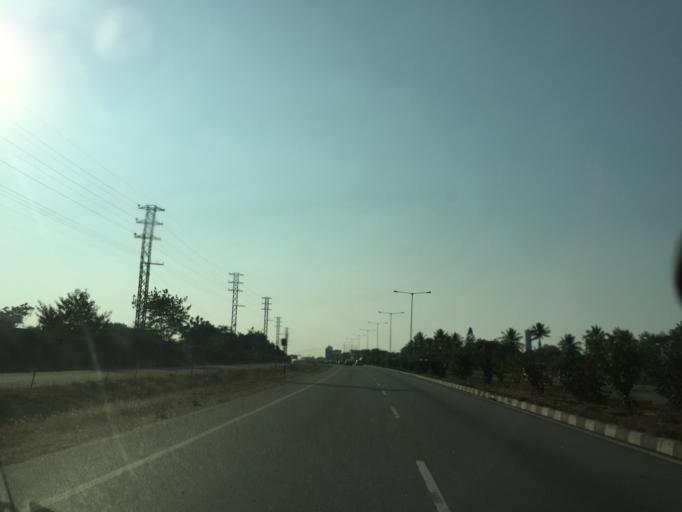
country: IN
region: Telangana
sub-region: Nalgonda
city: Bhongir
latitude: 17.5045
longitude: 78.8676
